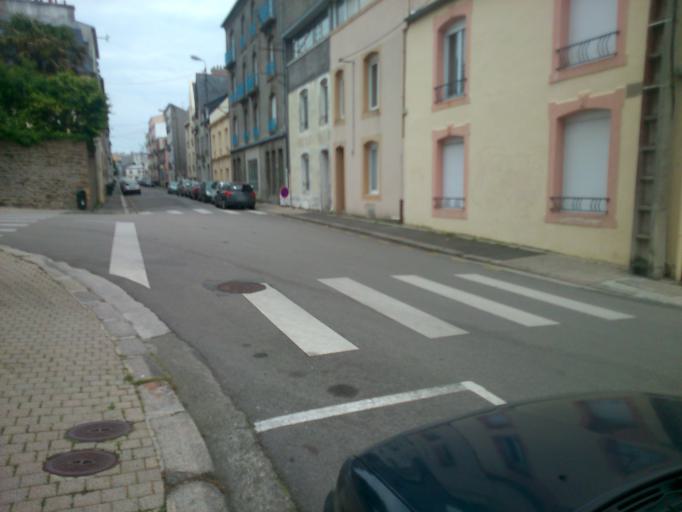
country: FR
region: Brittany
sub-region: Departement du Finistere
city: Brest
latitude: 48.3916
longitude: -4.4761
